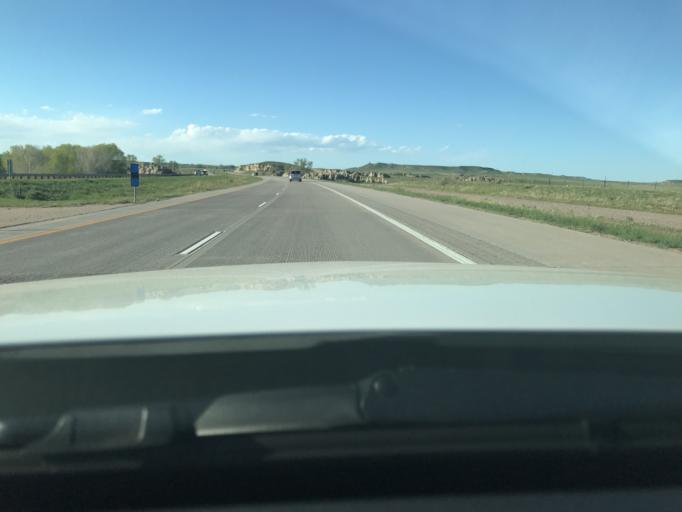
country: US
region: Wyoming
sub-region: Laramie County
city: South Greeley
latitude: 40.9496
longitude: -104.9243
